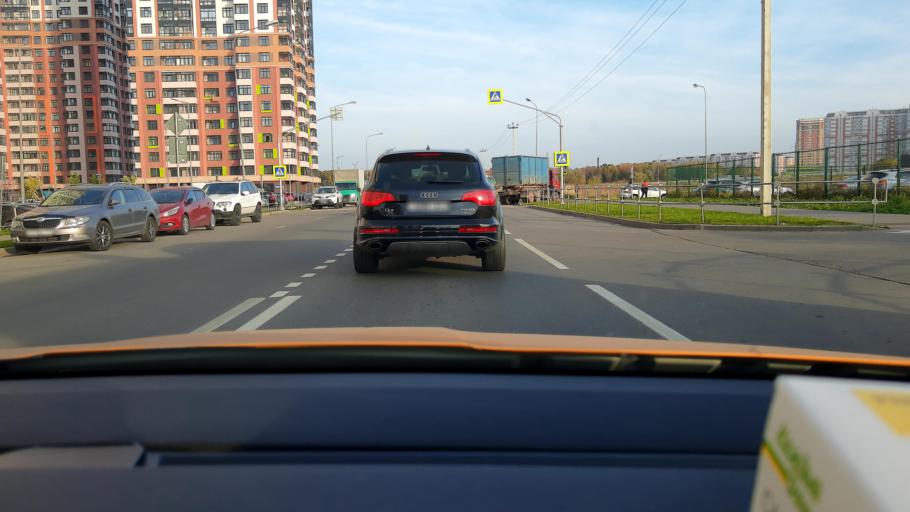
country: RU
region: Moskovskaya
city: Moskovskiy
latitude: 55.5981
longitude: 37.3620
